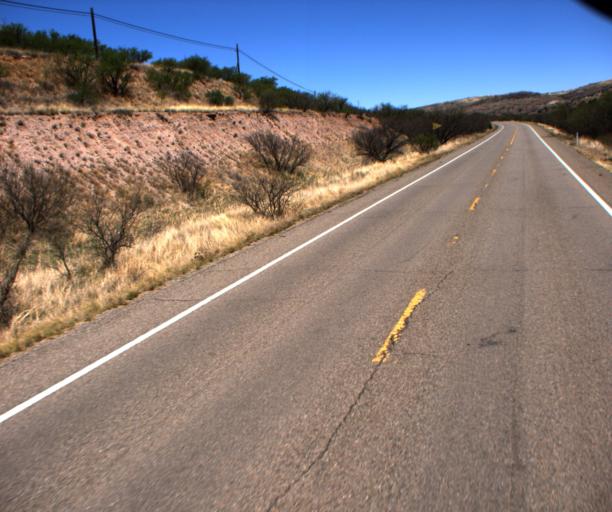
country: US
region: Arizona
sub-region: Santa Cruz County
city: Rio Rico
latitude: 31.6241
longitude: -110.7170
